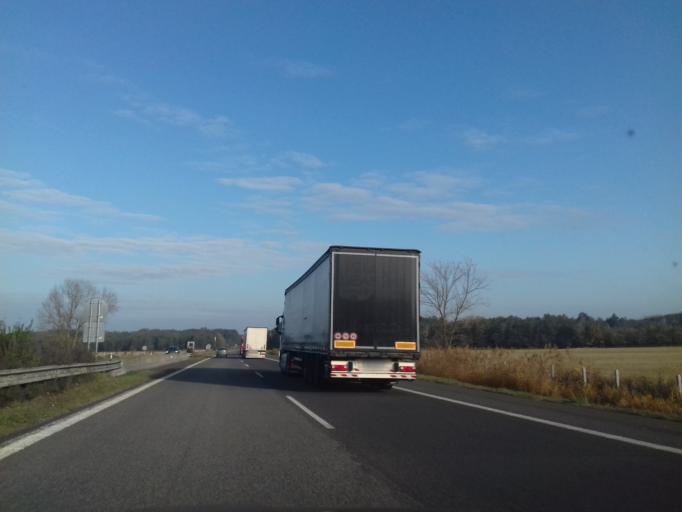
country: SK
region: Bratislavsky
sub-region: Okres Malacky
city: Malacky
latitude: 48.4667
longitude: 17.0354
